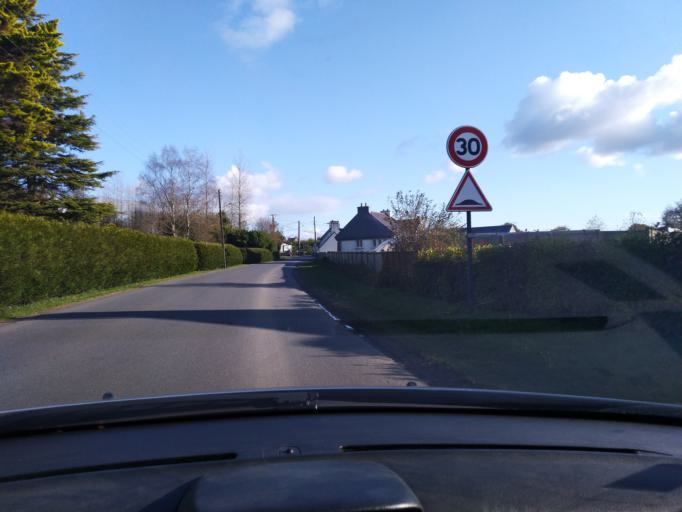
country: FR
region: Brittany
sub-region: Departement des Cotes-d'Armor
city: Plestin-les-Greves
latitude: 48.6073
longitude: -3.6184
